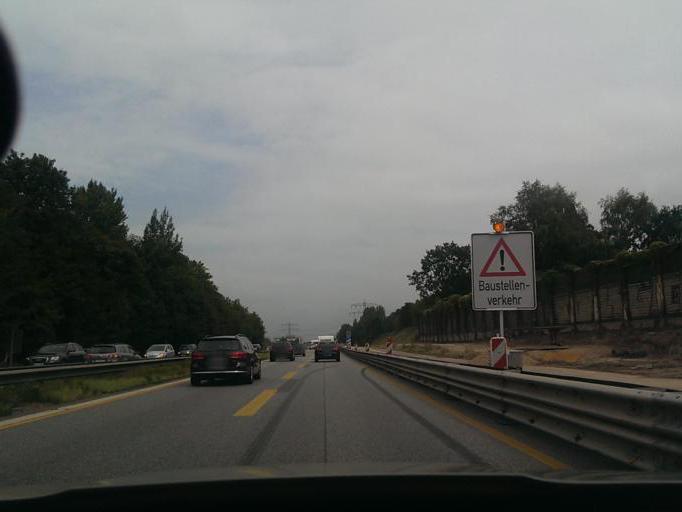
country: DE
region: Schleswig-Holstein
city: Bonningstedt
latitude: 53.6390
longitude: 9.9265
